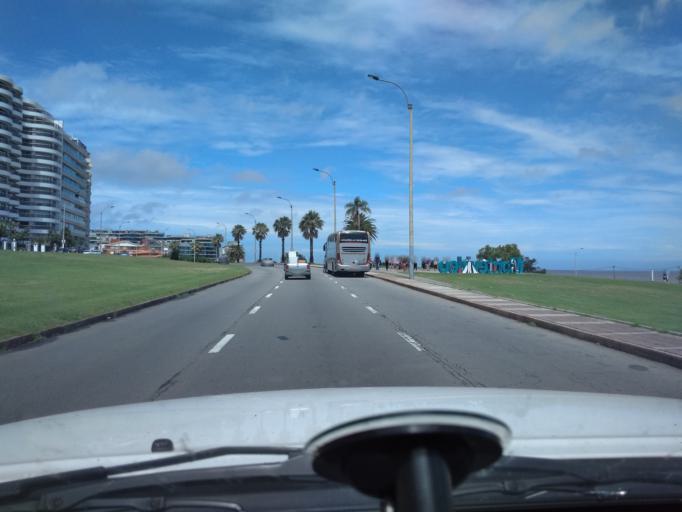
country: UY
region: Montevideo
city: Montevideo
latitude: -34.9101
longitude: -56.1392
